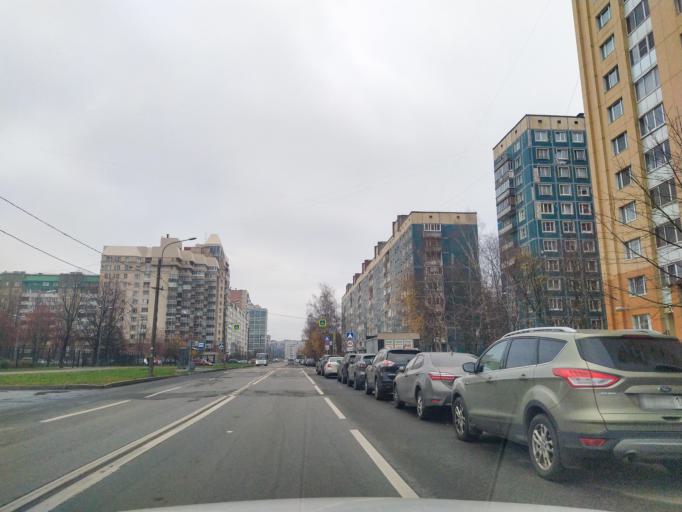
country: RU
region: St.-Petersburg
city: Ozerki
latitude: 60.0349
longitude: 30.3300
